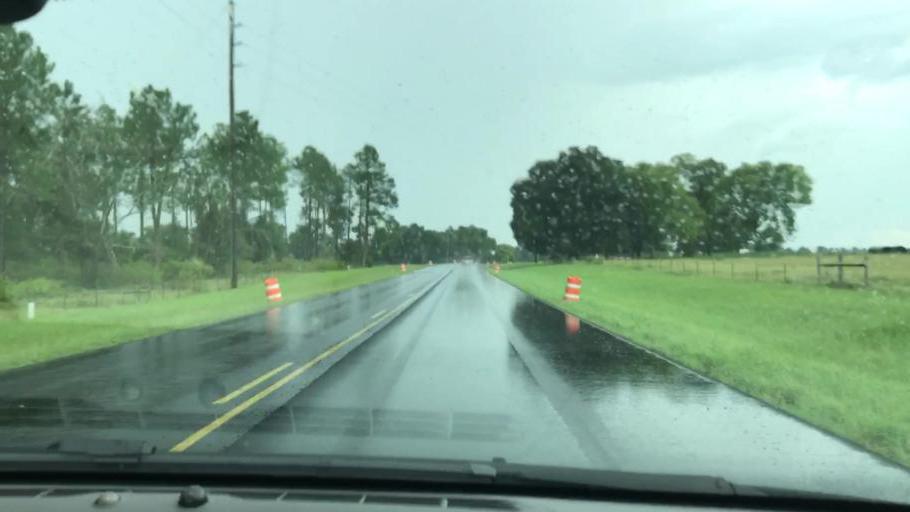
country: US
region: Georgia
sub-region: Clay County
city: Fort Gaines
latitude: 31.5361
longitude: -85.0212
